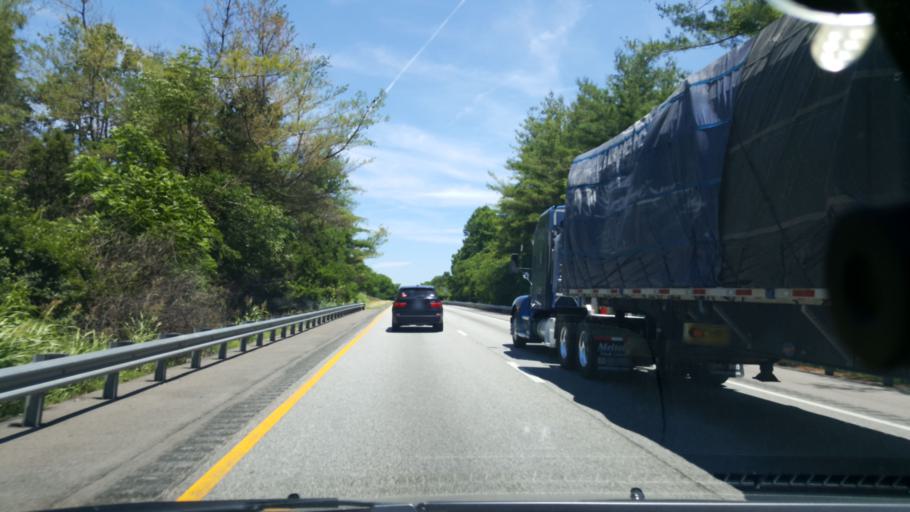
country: US
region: Virginia
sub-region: Botetourt County
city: Fincastle
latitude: 37.4606
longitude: -79.8292
